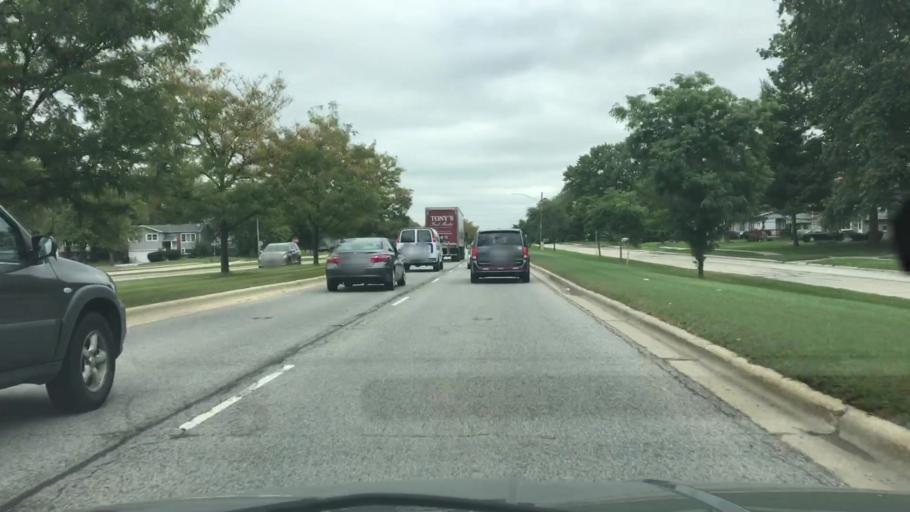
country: US
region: Illinois
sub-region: DuPage County
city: Woodridge
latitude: 41.7501
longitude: -88.0501
